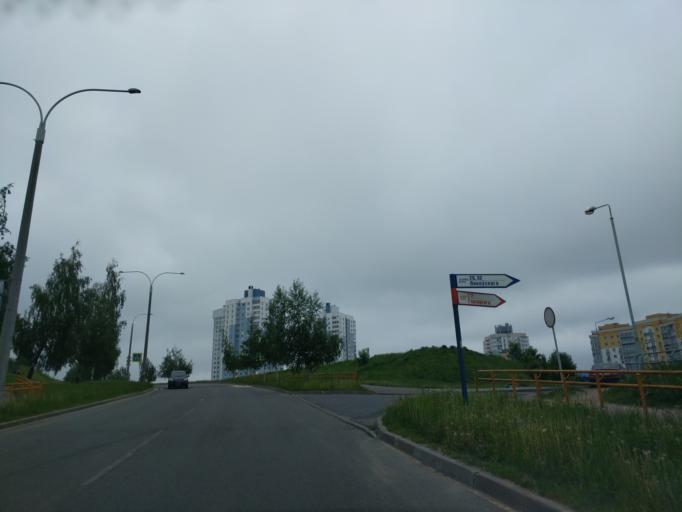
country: BY
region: Minsk
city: Novoye Medvezhino
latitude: 53.8784
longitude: 27.4502
